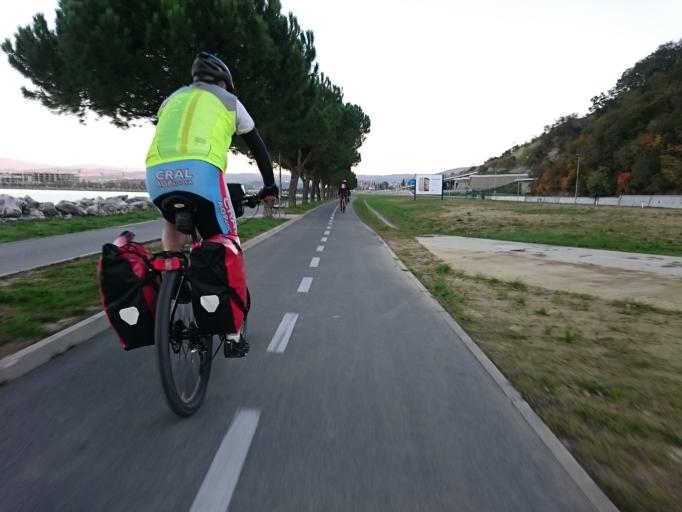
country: SI
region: Koper-Capodistria
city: Koper
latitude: 45.5451
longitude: 13.7139
